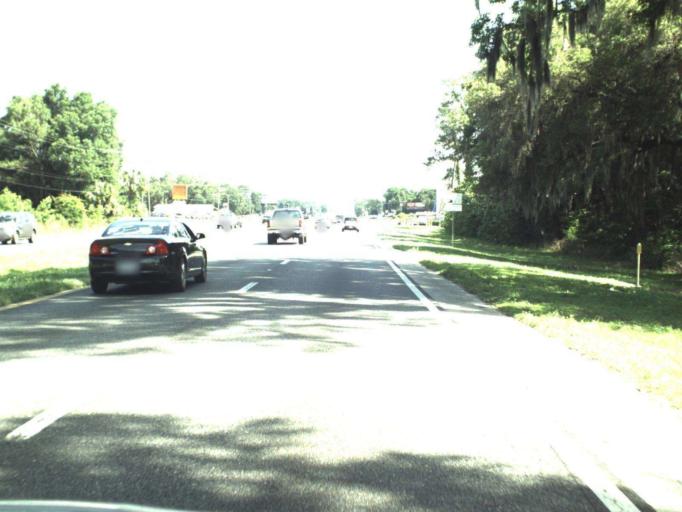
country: US
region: Florida
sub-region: Marion County
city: Ocala
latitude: 29.1424
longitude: -82.1120
